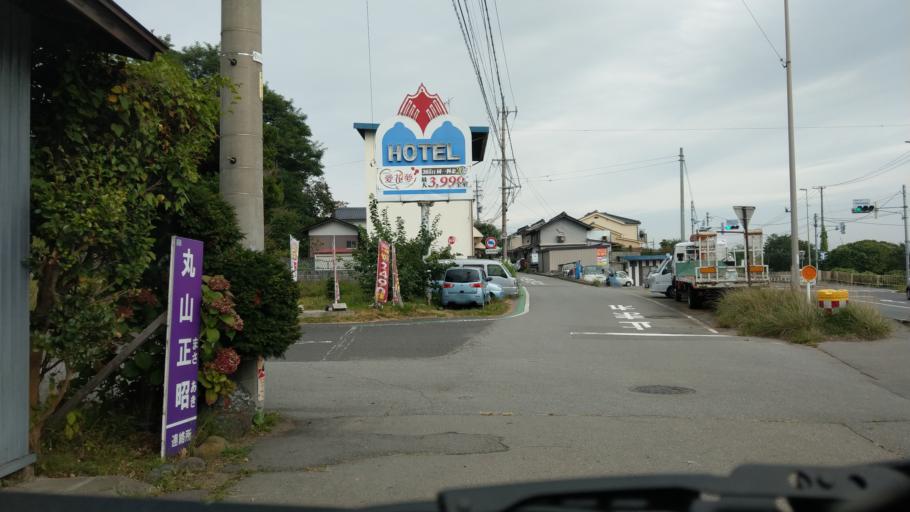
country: JP
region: Nagano
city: Komoro
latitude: 36.3399
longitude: 138.3950
